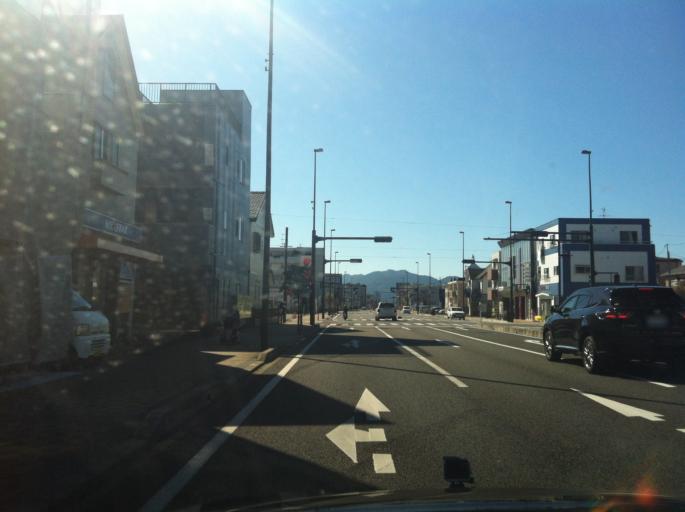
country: JP
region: Shizuoka
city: Shizuoka-shi
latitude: 34.9677
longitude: 138.4026
